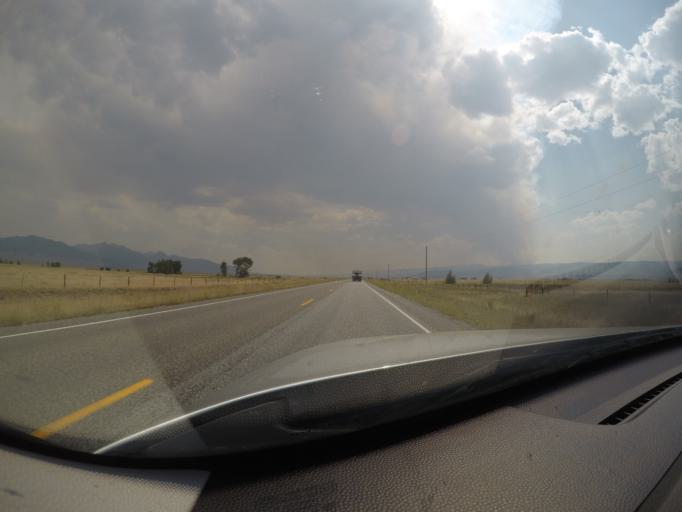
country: US
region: Montana
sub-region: Madison County
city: Virginia City
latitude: 45.1876
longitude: -111.6789
